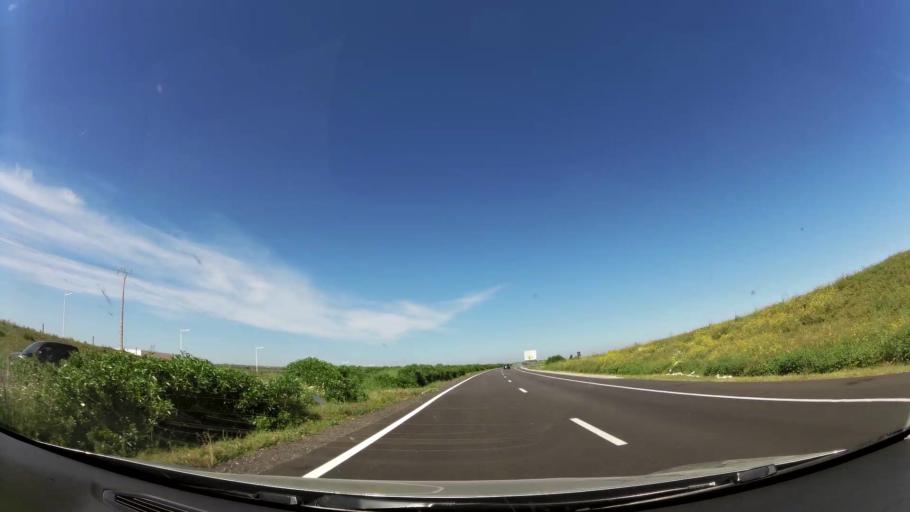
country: MA
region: Meknes-Tafilalet
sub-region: Meknes
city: Meknes
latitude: 33.8333
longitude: -5.4729
